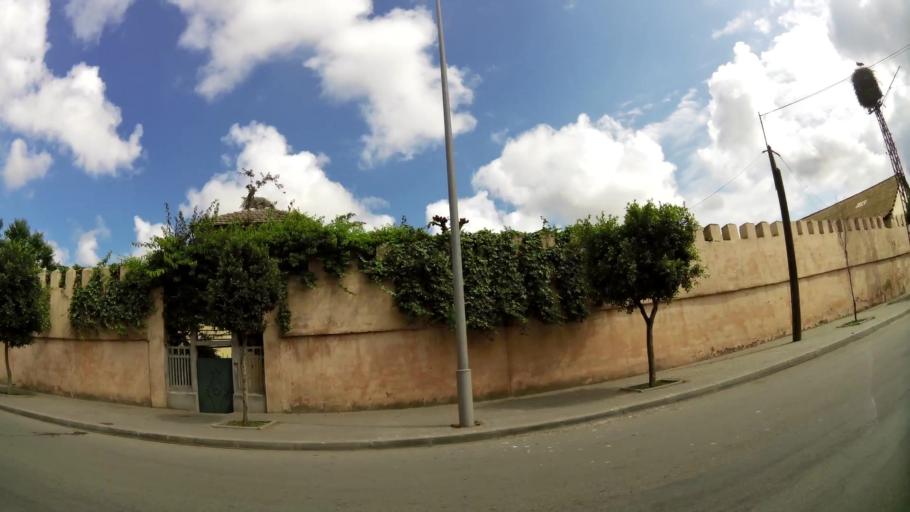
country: MA
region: Gharb-Chrarda-Beni Hssen
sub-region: Kenitra Province
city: Kenitra
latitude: 34.2669
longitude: -6.5746
